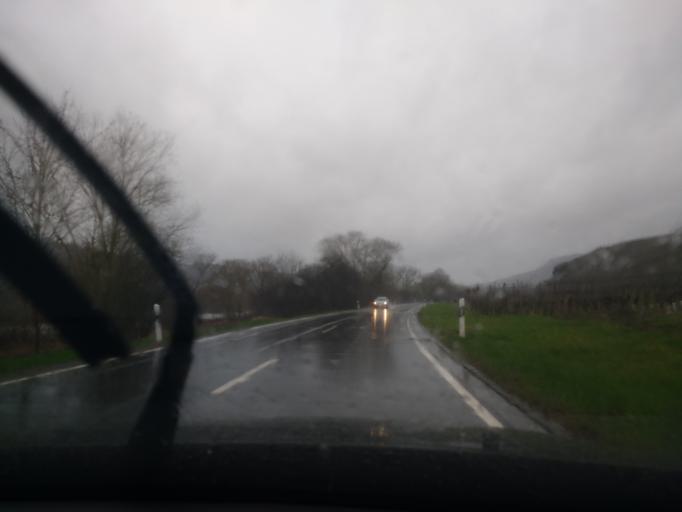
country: DE
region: Rheinland-Pfalz
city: Krov
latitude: 49.9687
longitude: 7.0712
